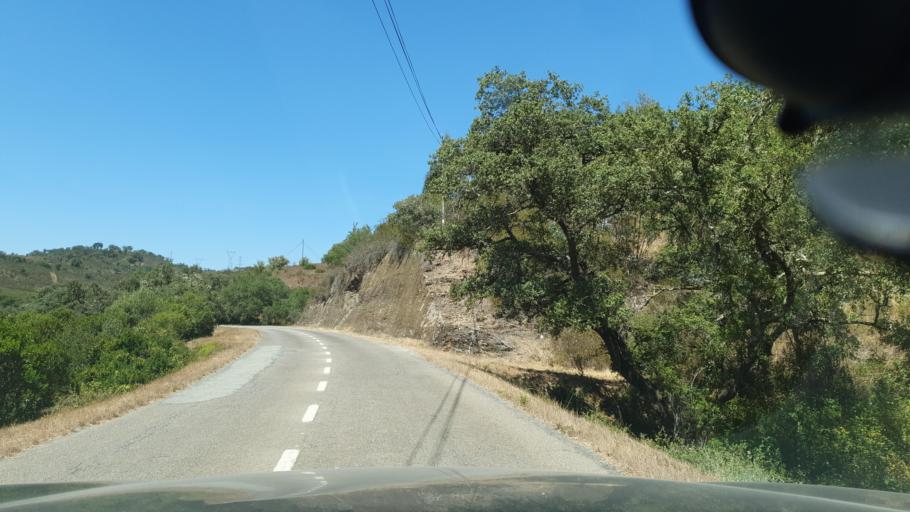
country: PT
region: Beja
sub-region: Odemira
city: Odemira
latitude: 37.6045
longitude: -8.5928
